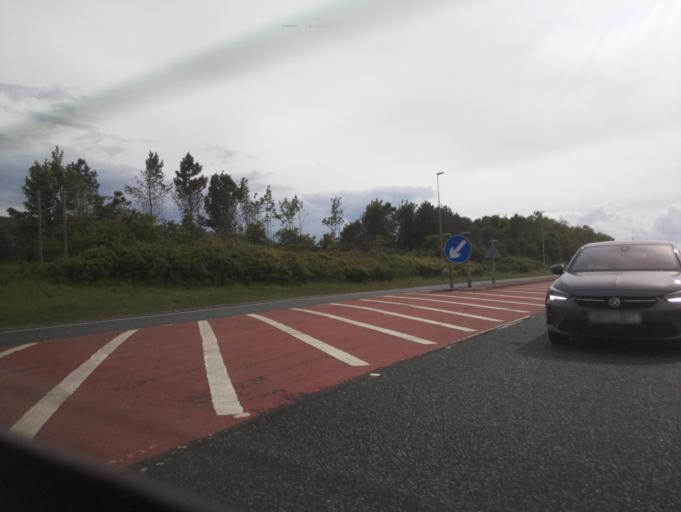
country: GB
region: England
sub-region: Northumberland
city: Berwick-Upon-Tweed
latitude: 55.7829
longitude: -2.0221
